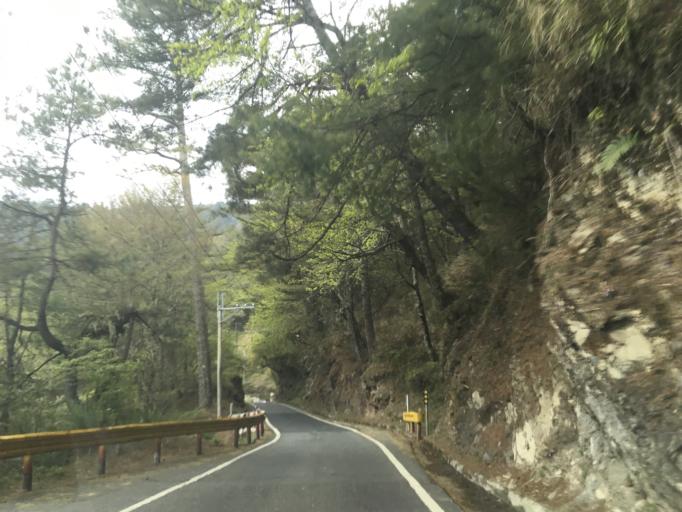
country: TW
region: Taiwan
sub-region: Hualien
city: Hualian
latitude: 24.1872
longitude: 121.3296
